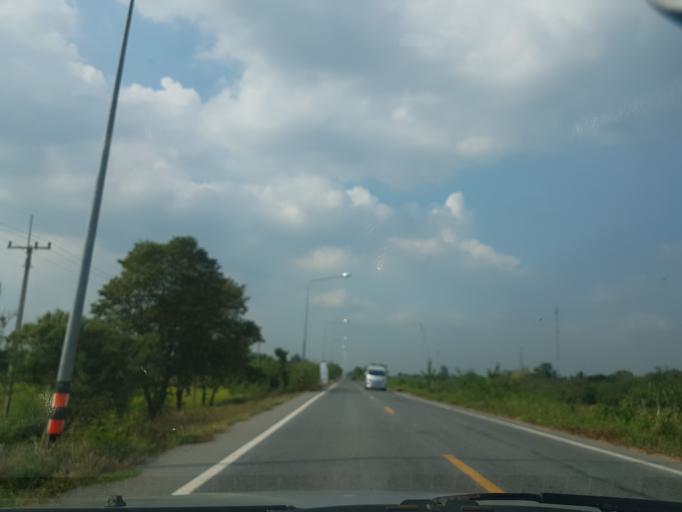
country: TH
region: Phra Nakhon Si Ayutthaya
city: Phachi
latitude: 14.4628
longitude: 100.7532
